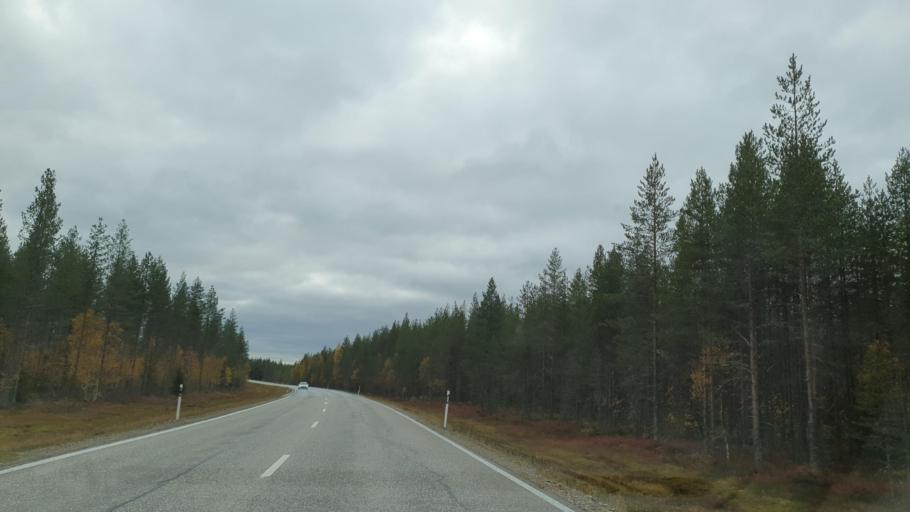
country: FI
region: Northern Ostrobothnia
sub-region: Oulunkaari
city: Pudasjaervi
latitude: 65.5308
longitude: 26.7610
